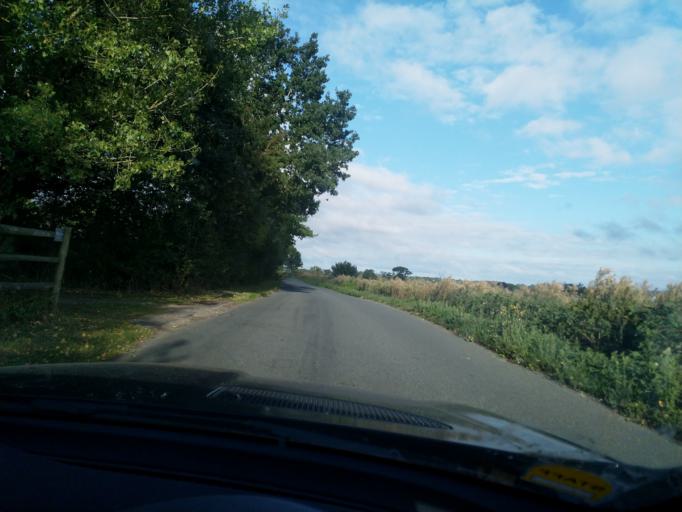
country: GB
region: England
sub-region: Suffolk
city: Elmswell
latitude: 52.2337
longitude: 0.9631
